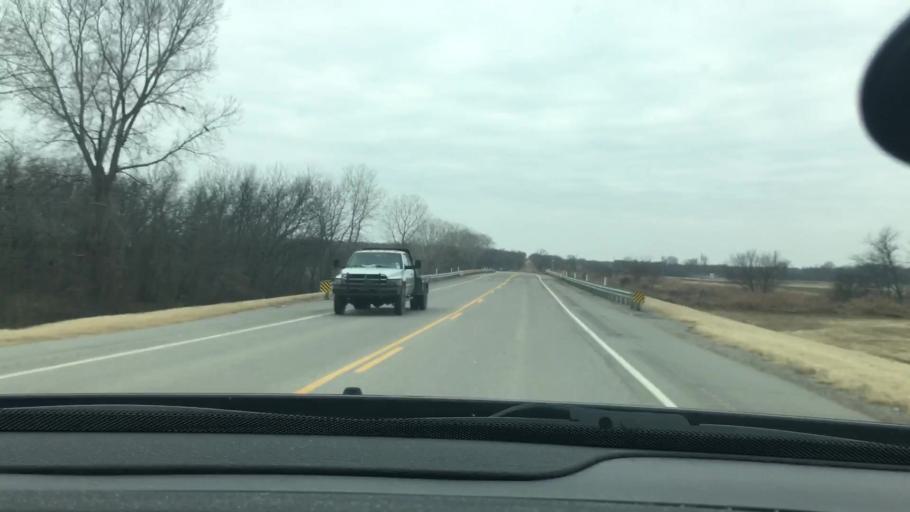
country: US
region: Oklahoma
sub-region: Carter County
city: Healdton
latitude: 34.4925
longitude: -97.4382
